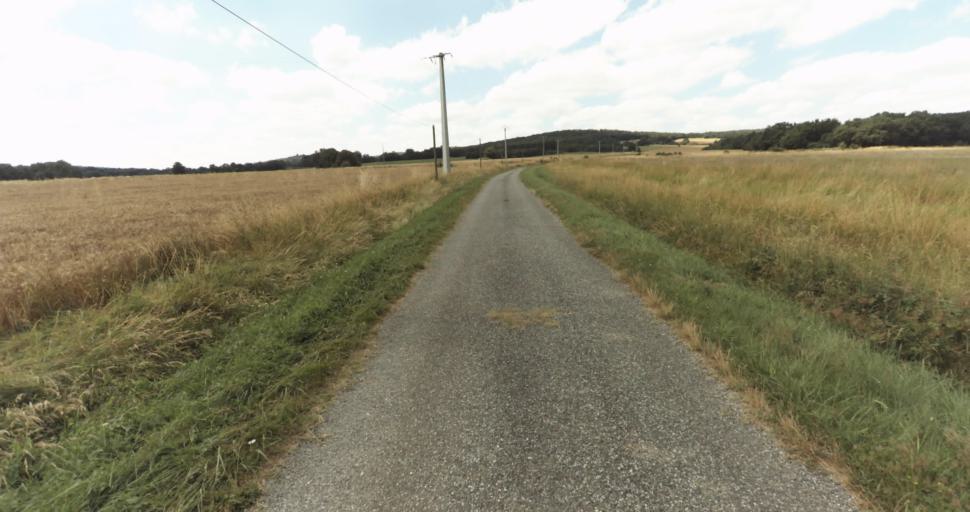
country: FR
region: Midi-Pyrenees
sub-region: Departement de la Haute-Garonne
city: Fontenilles
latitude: 43.5648
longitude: 1.1734
